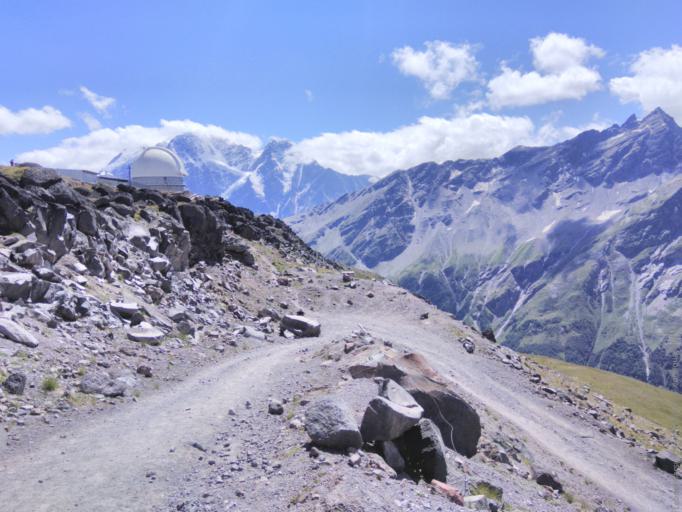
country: RU
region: Kabardino-Balkariya
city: Terskol
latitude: 43.2787
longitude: 42.4990
